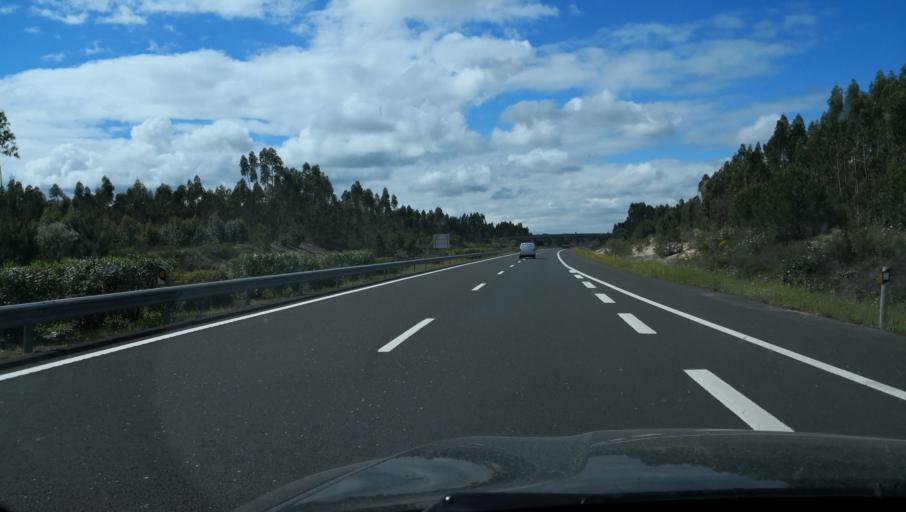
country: PT
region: Santarem
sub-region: Benavente
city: Poceirao
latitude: 38.7298
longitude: -8.6735
